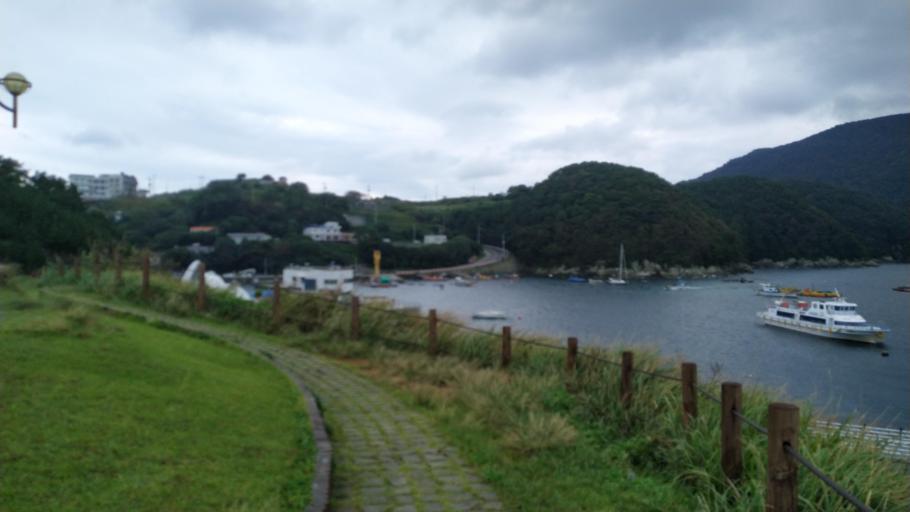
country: KR
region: Gyeongsangnam-do
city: Kyosai
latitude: 34.7448
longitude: 128.6630
